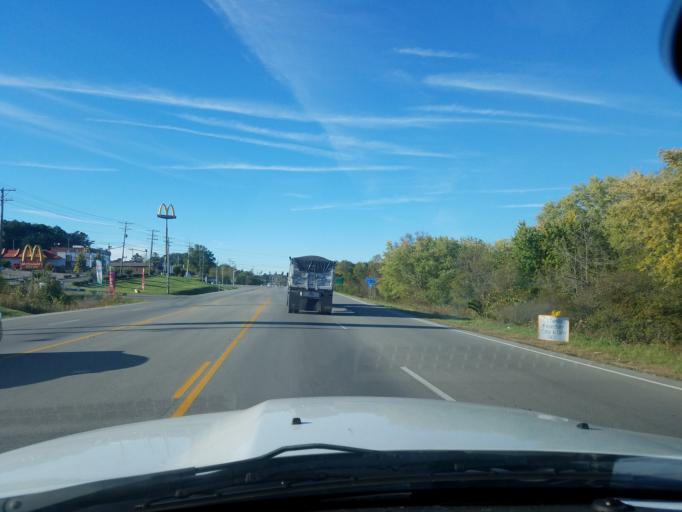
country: US
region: Kentucky
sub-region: Laurel County
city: London
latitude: 37.1054
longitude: -84.0713
